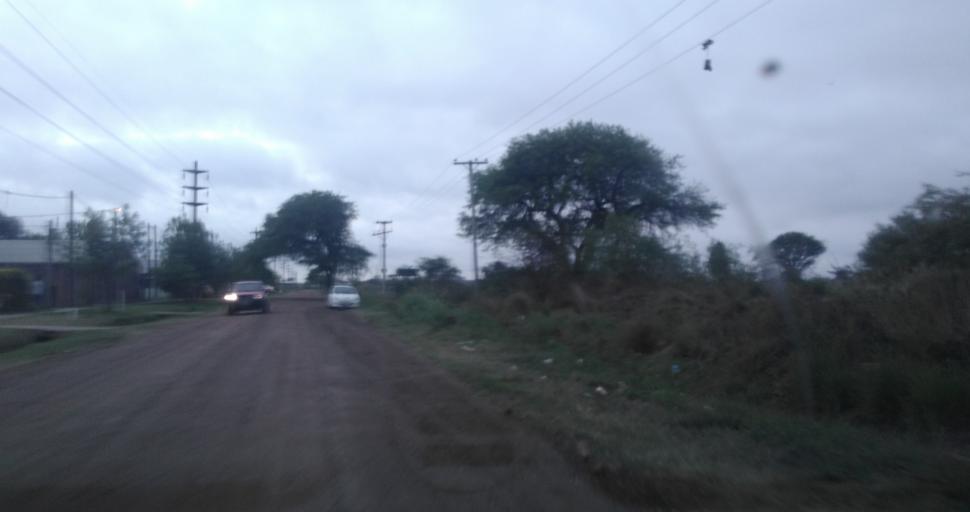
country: AR
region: Chaco
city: Fontana
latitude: -27.3975
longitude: -59.0001
